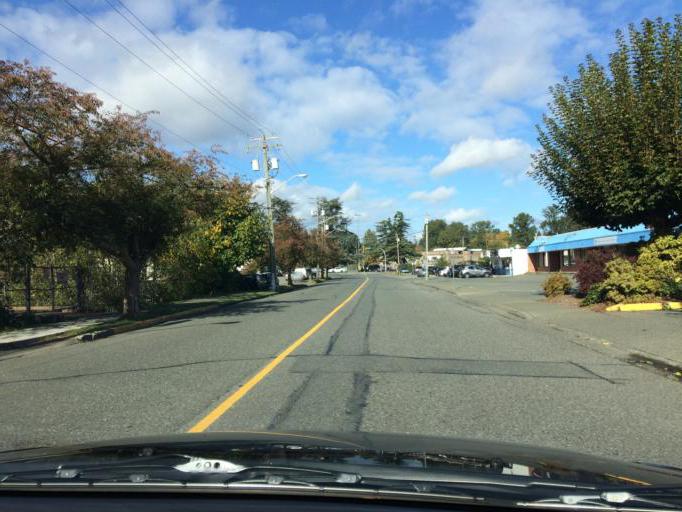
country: CA
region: British Columbia
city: Courtenay
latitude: 49.6926
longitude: -124.9914
